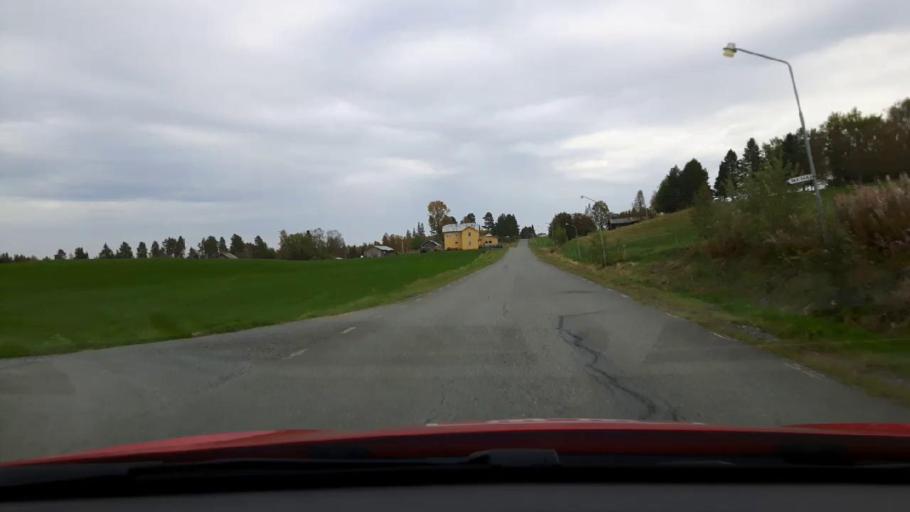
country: SE
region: Jaemtland
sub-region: Krokoms Kommun
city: Krokom
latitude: 63.2321
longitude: 14.1245
